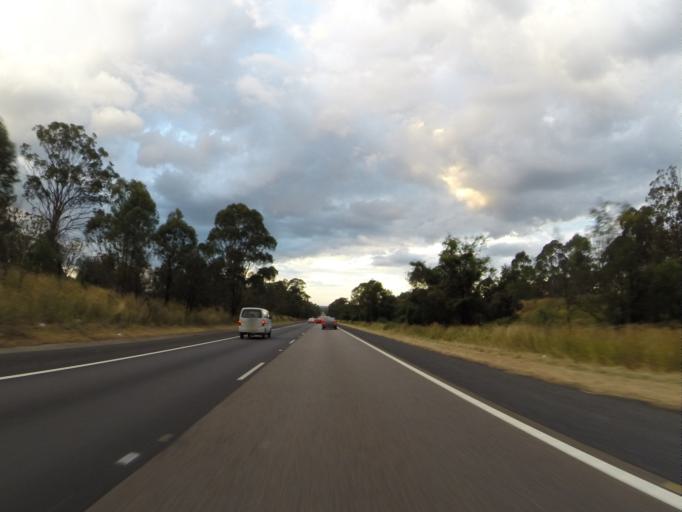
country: AU
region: New South Wales
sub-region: Wollondilly
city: Douglas Park
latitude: -34.2144
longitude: 150.6850
